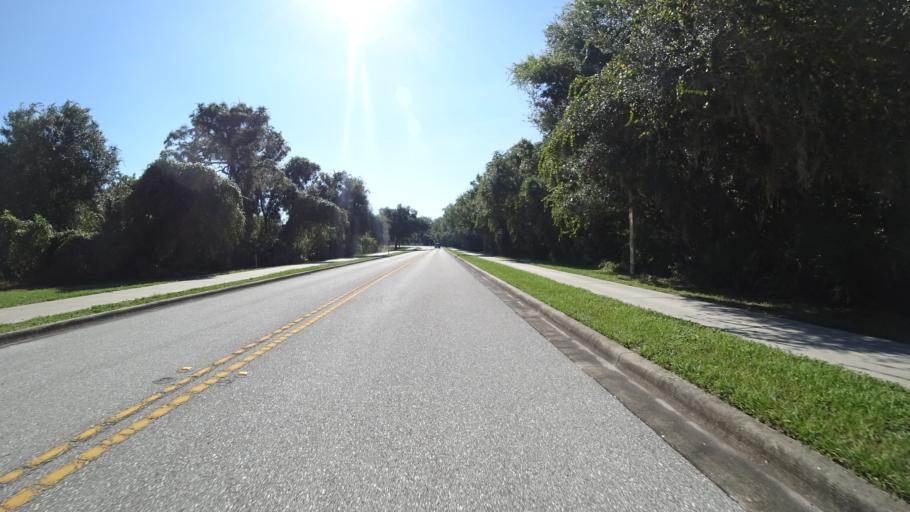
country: US
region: Florida
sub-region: Sarasota County
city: The Meadows
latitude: 27.4198
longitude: -82.4339
